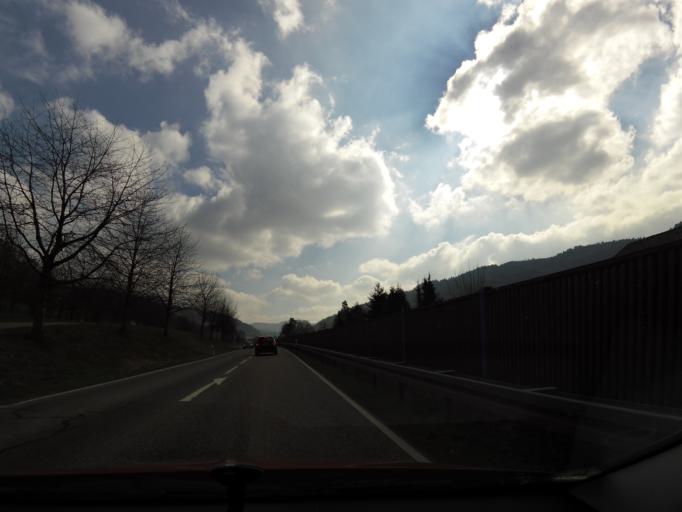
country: DE
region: Baden-Wuerttemberg
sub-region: Freiburg Region
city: Kappelrodeck
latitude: 48.5861
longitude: 8.1269
